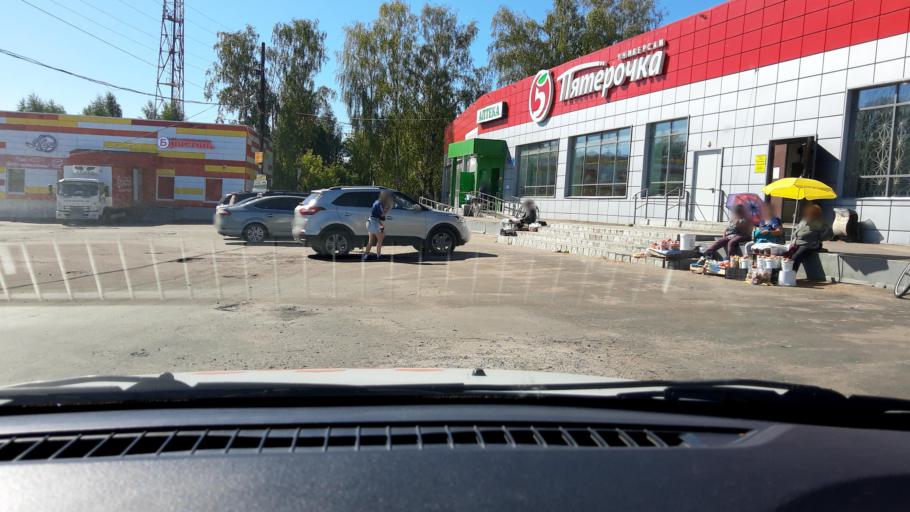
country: RU
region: Nizjnij Novgorod
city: Zavolzh'ye
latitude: 56.7161
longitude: 43.4141
